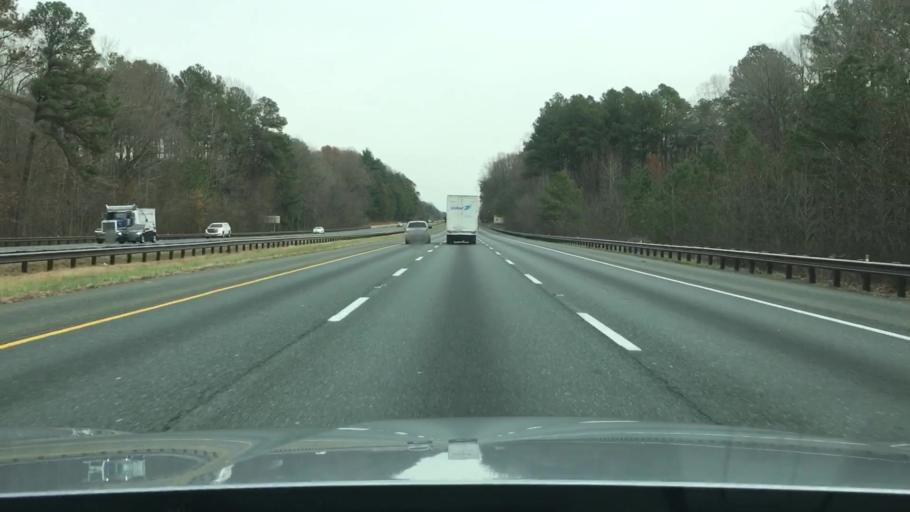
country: US
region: Maryland
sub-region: Anne Arundel County
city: Crofton
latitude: 38.9572
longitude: -76.6710
